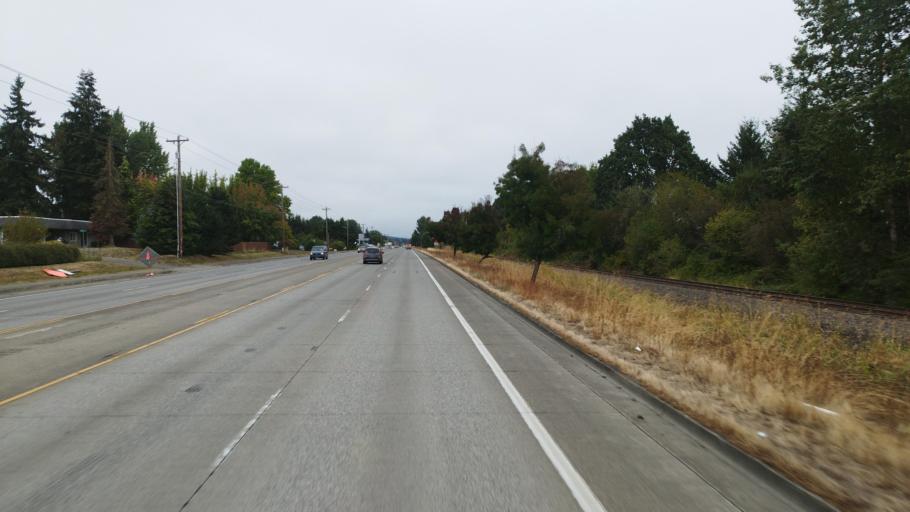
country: US
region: Oregon
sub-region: Columbia County
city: Warren
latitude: 45.8319
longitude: -122.8412
